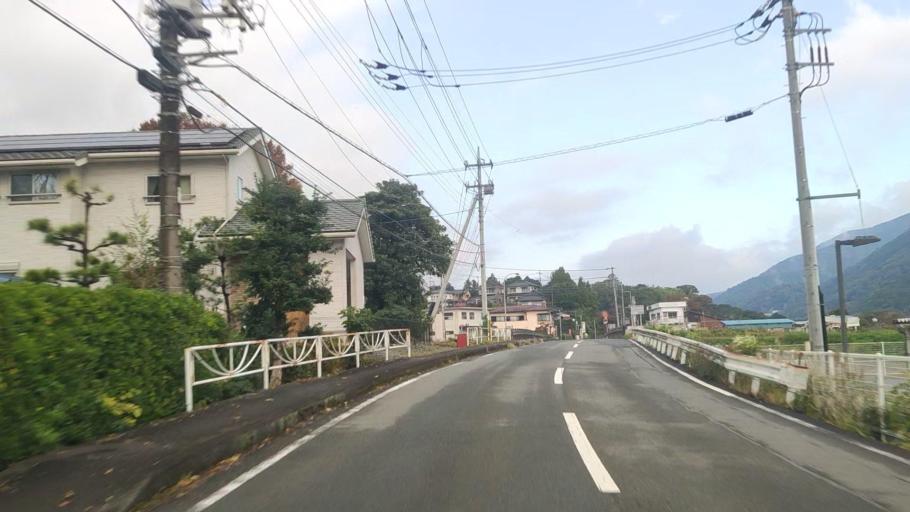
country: JP
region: Shizuoka
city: Fujinomiya
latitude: 35.2972
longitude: 138.4509
